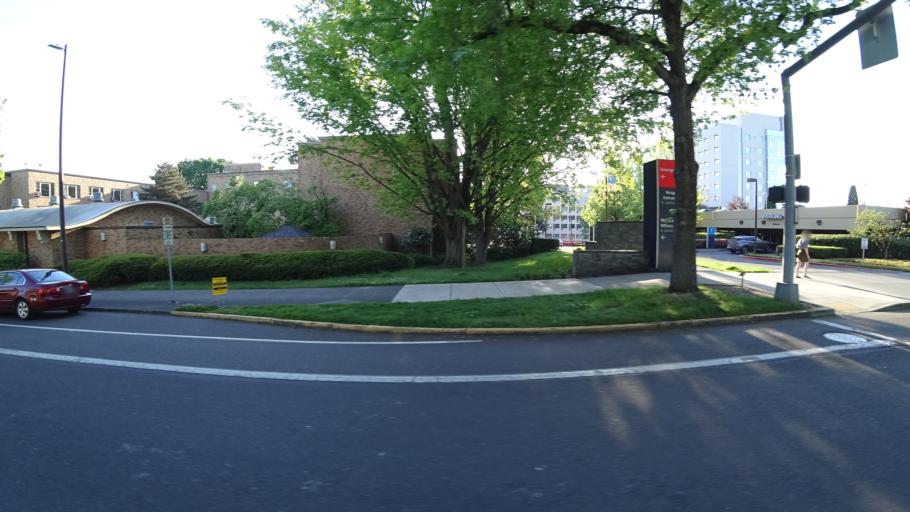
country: US
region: Oregon
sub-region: Multnomah County
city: Portland
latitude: 45.5437
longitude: -122.6681
